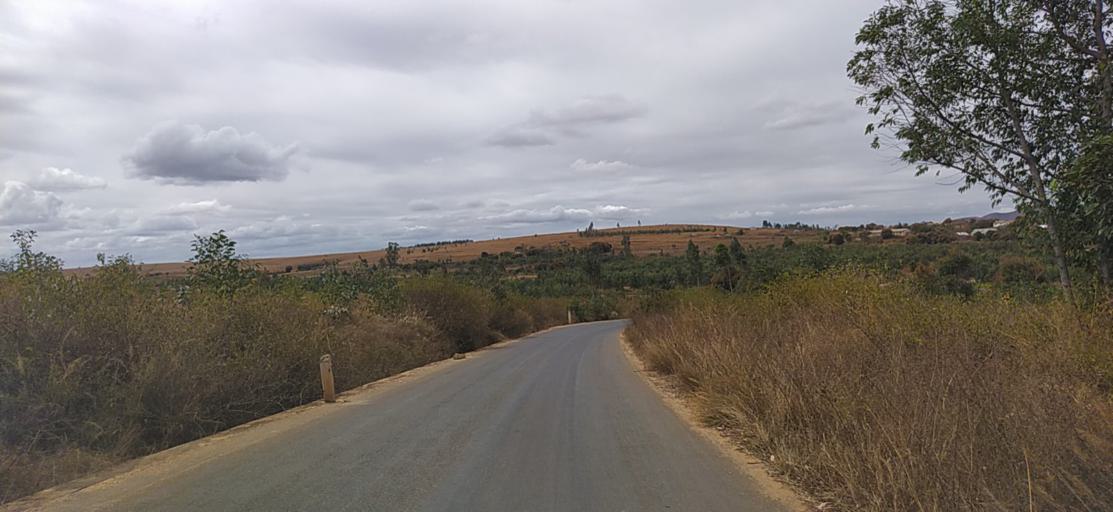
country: MG
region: Alaotra Mangoro
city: Ambatondrazaka
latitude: -17.9325
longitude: 48.2523
